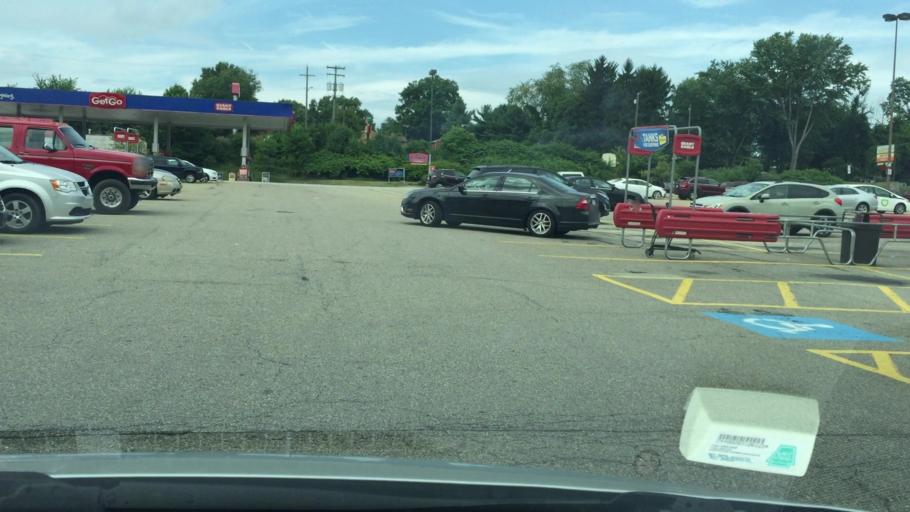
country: US
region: Pennsylvania
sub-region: Allegheny County
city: Tarentum
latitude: 40.5920
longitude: -79.7500
